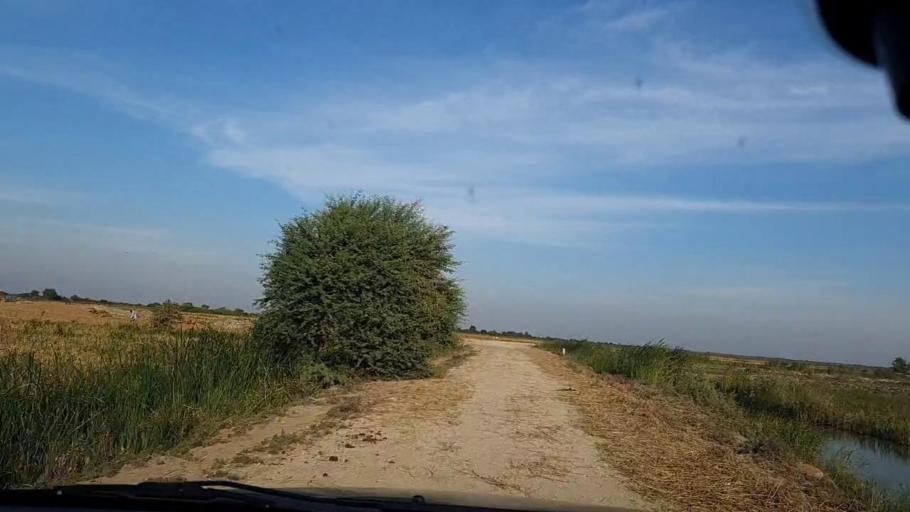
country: PK
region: Sindh
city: Mirpur Batoro
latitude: 24.6584
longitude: 68.3007
